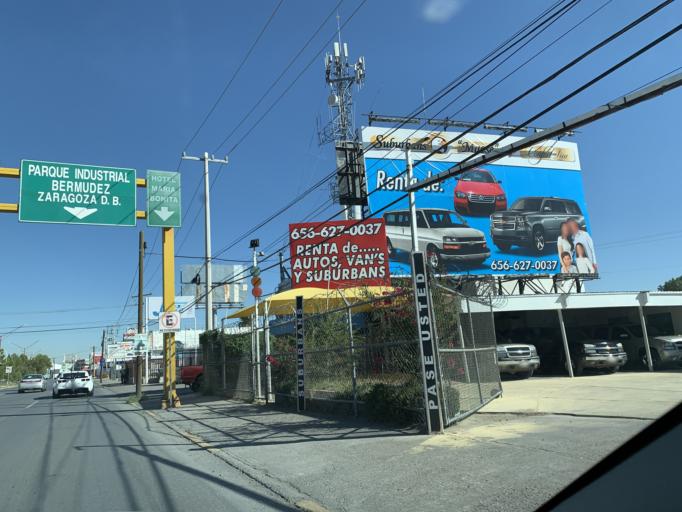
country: MX
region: Chihuahua
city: Ciudad Juarez
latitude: 31.7489
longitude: -106.4261
